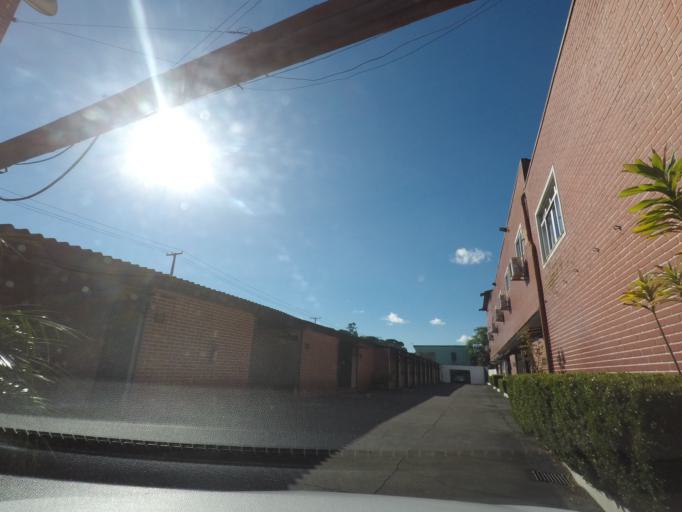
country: BR
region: Parana
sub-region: Almirante Tamandare
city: Almirante Tamandare
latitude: -25.3431
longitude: -49.2828
